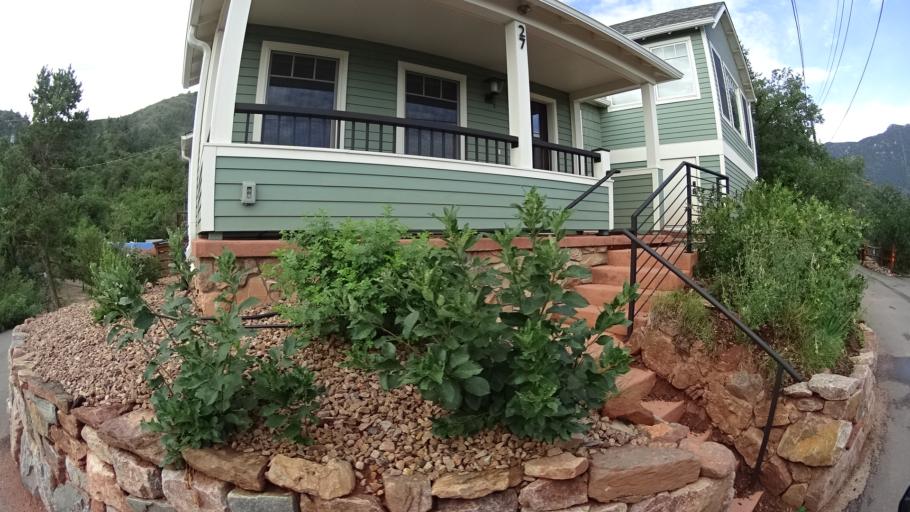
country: US
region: Colorado
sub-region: El Paso County
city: Manitou Springs
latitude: 38.8541
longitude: -104.9119
